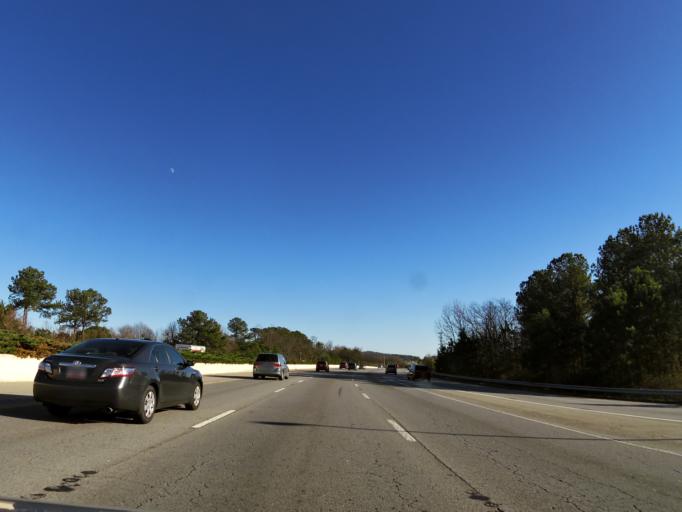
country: US
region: South Carolina
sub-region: Greenville County
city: Wade Hampton
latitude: 34.8538
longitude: -82.3328
